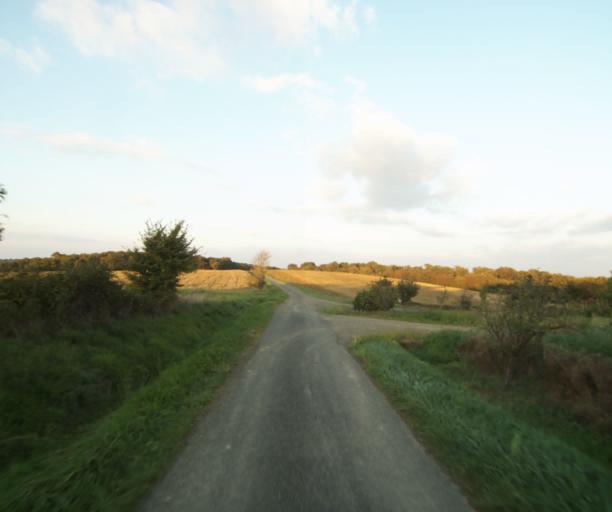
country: FR
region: Midi-Pyrenees
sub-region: Departement du Gers
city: Vic-Fezensac
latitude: 43.7806
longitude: 0.2059
